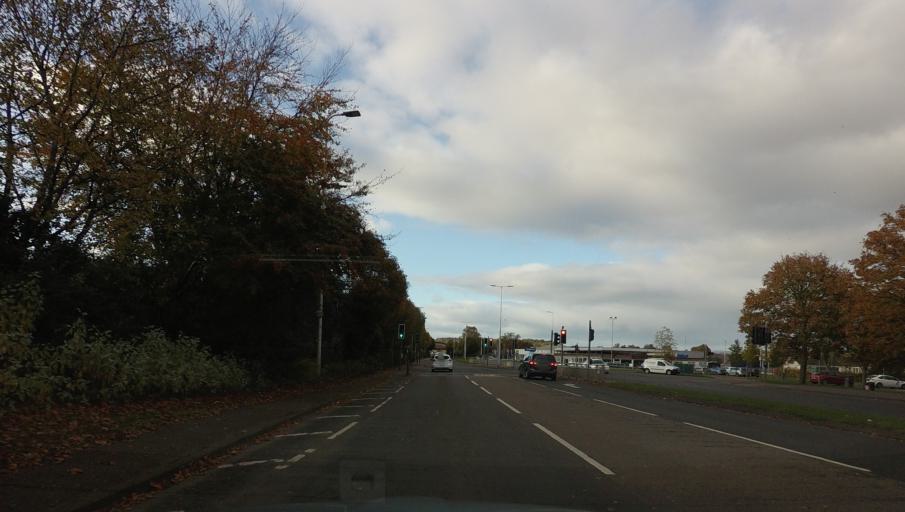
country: GB
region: Scotland
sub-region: Perth and Kinross
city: Perth
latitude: 56.4135
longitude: -3.4572
